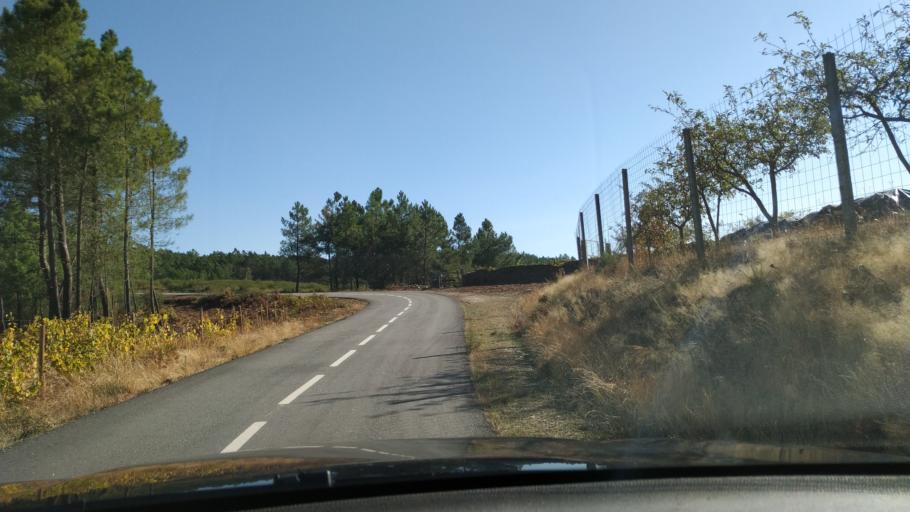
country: PT
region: Vila Real
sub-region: Sabrosa
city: Vilela
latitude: 41.2278
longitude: -7.6259
